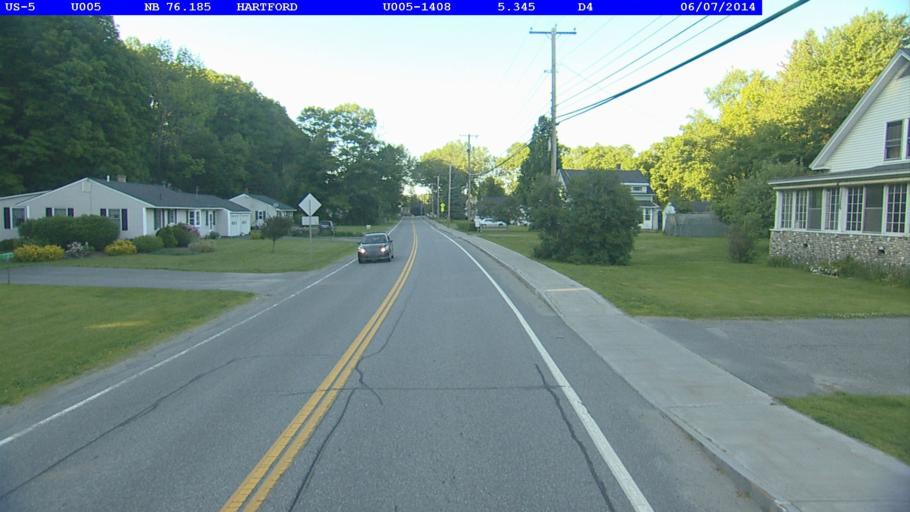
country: US
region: Vermont
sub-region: Windsor County
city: Wilder
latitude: 43.6690
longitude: -72.3108
